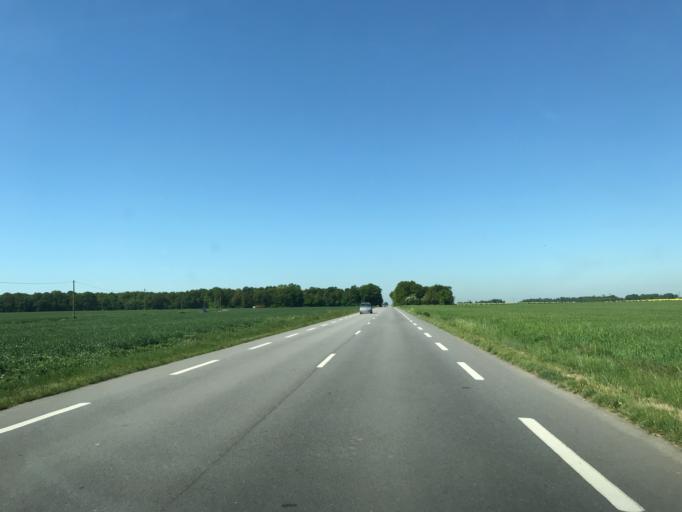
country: FR
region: Haute-Normandie
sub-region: Departement de l'Eure
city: La Madeleine-de-Nonancourt
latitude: 48.8970
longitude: 1.2281
